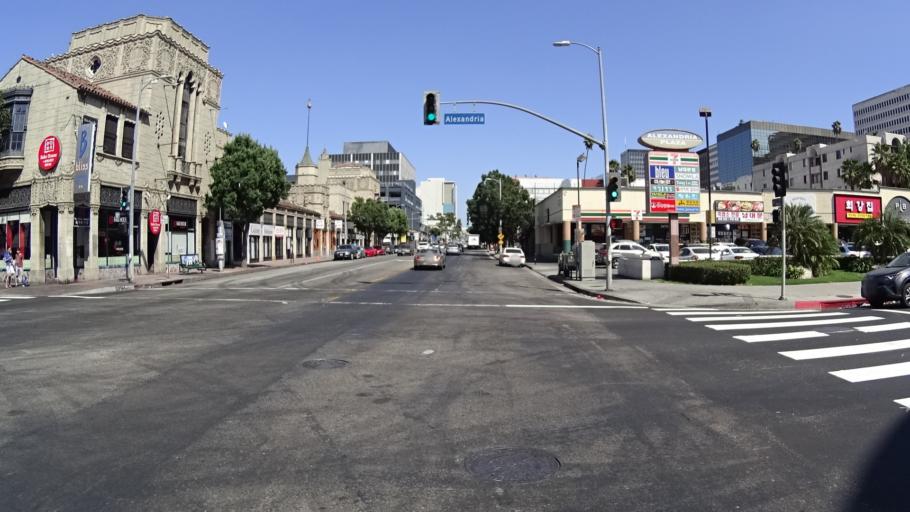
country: US
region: California
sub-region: Los Angeles County
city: Silver Lake
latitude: 34.0635
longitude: -118.2981
